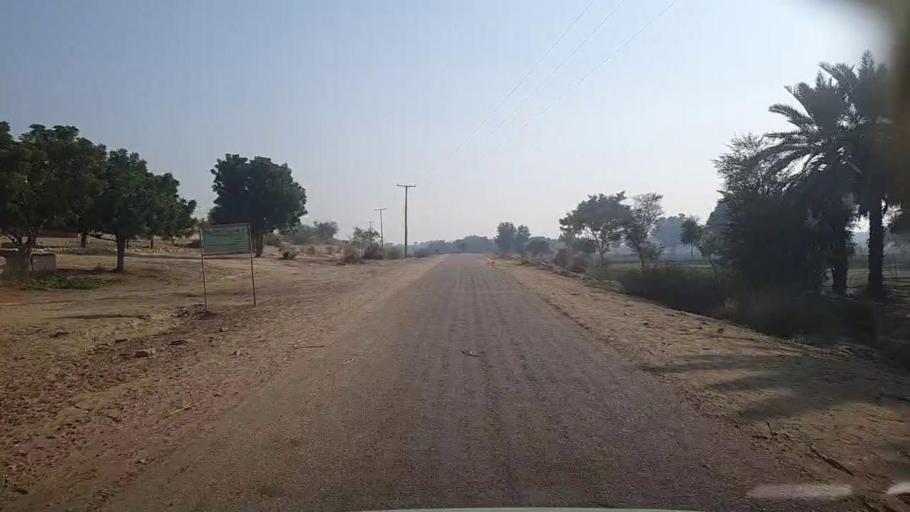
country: PK
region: Sindh
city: Kandiari
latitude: 26.8358
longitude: 68.4895
